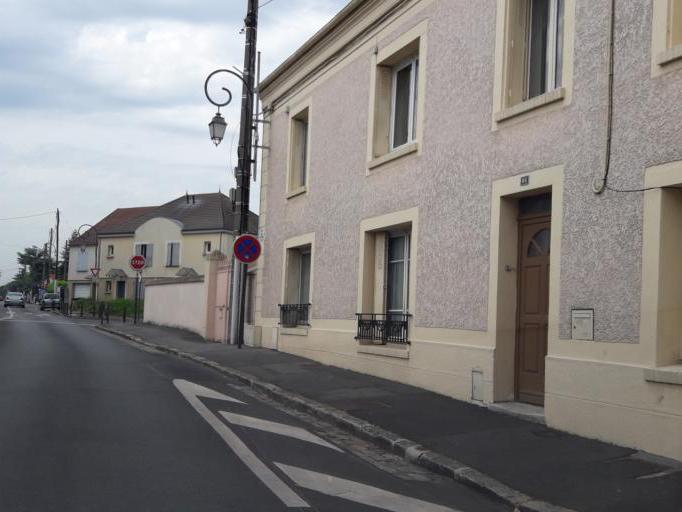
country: FR
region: Ile-de-France
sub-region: Departement de l'Essonne
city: Morsang-sur-Orge
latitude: 48.6624
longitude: 2.3483
